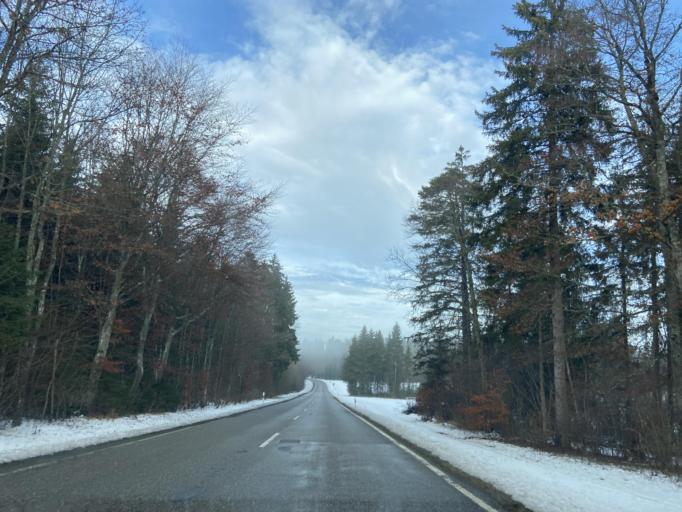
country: DE
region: Baden-Wuerttemberg
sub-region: Tuebingen Region
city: Hettingen
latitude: 48.2303
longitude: 9.2841
